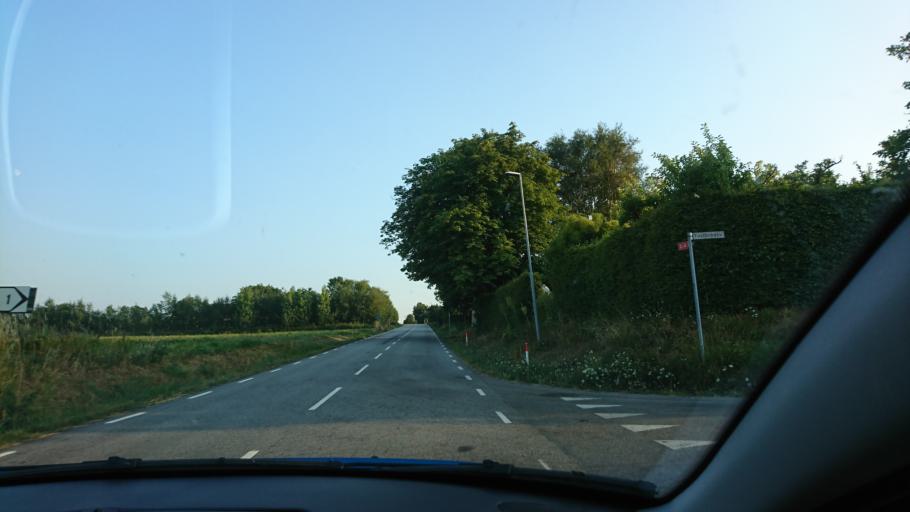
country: SE
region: Skane
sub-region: Simrishamns Kommun
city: Kivik
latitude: 55.7078
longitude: 14.1517
